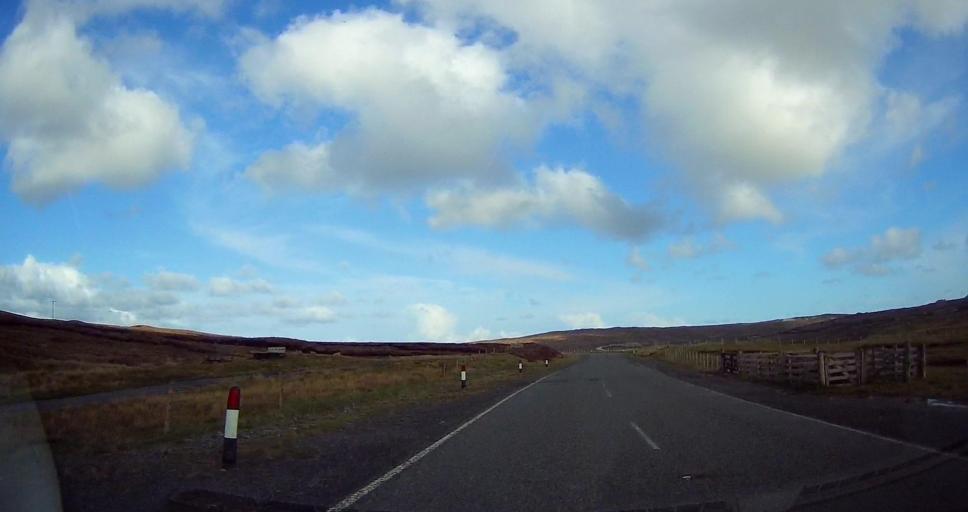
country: GB
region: Scotland
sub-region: Shetland Islands
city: Lerwick
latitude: 60.3495
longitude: -1.2319
